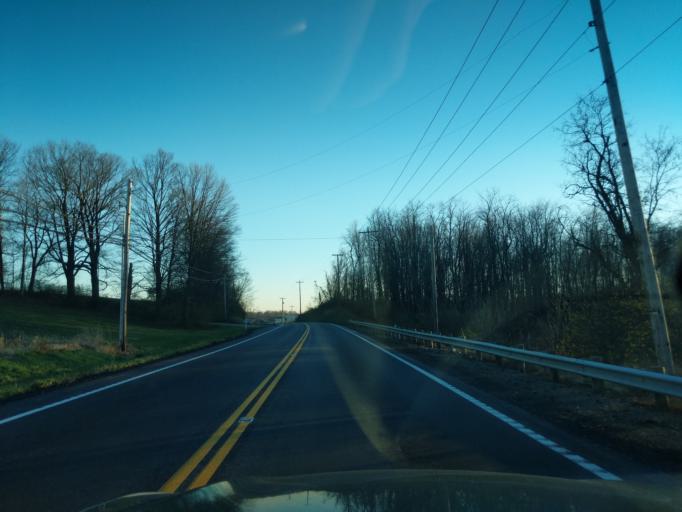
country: US
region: Ohio
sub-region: Licking County
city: Newark
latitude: 40.0266
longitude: -82.4026
